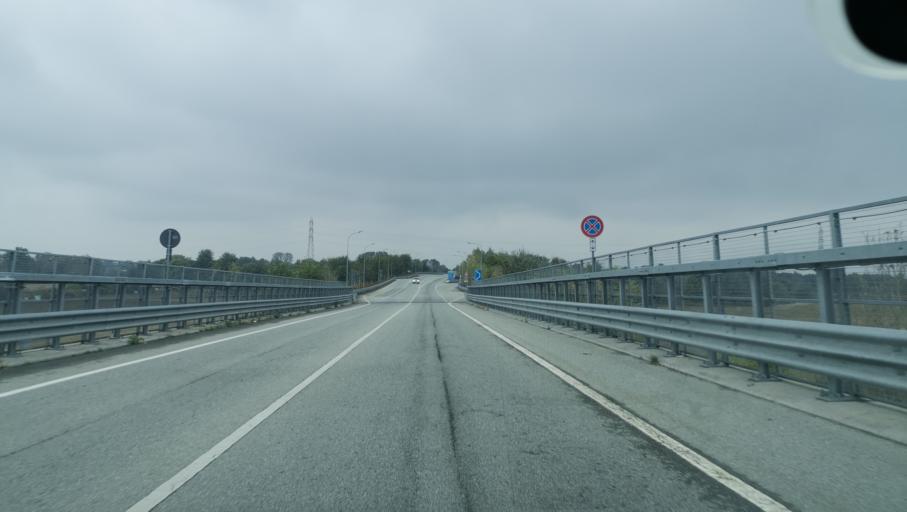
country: IT
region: Piedmont
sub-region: Provincia di Torino
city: Brandizzo
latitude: 45.1583
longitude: 7.8270
